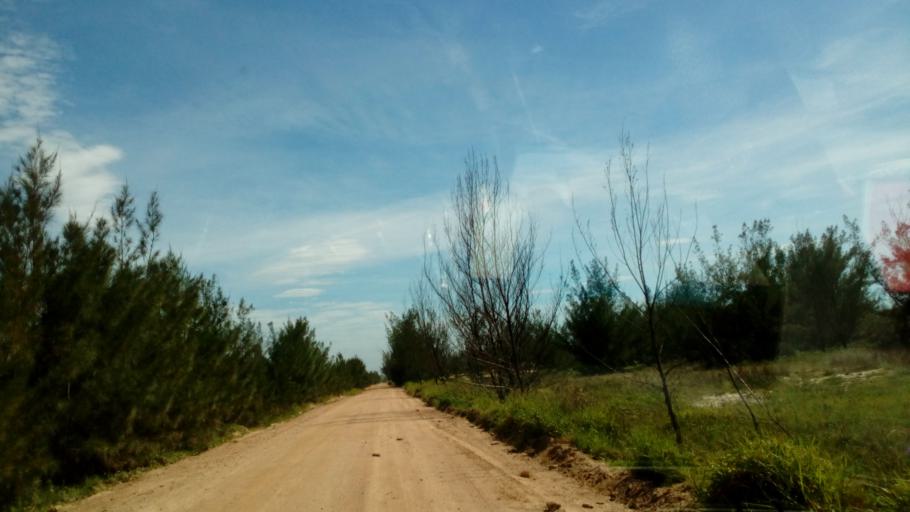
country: BR
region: Santa Catarina
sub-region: Laguna
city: Laguna
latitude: -28.4540
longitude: -48.7650
